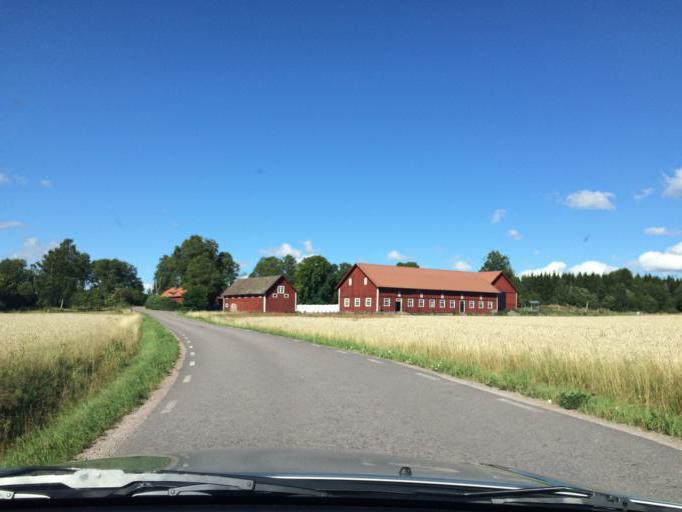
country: SE
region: Soedermanland
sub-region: Eskilstuna Kommun
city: Kvicksund
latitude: 59.5057
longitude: 16.3818
